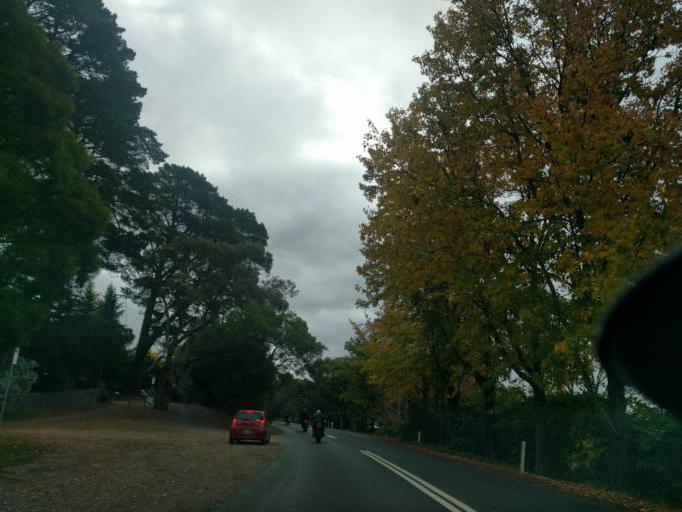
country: AU
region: South Australia
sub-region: Adelaide Hills
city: Stirling
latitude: -35.0175
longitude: 138.7495
